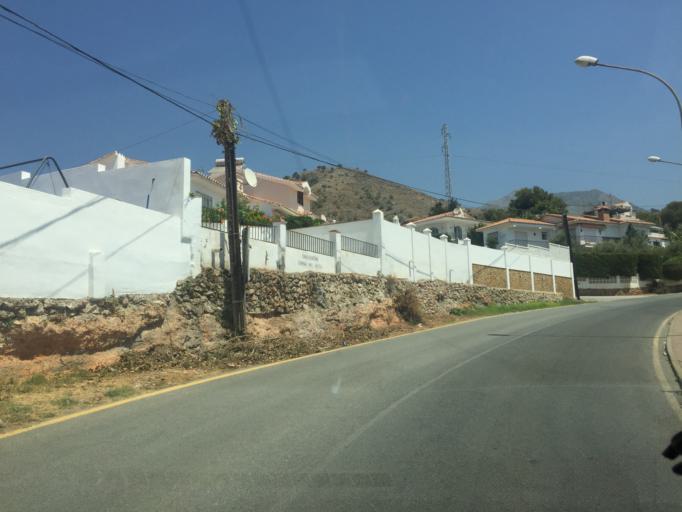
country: ES
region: Andalusia
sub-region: Provincia de Malaga
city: Nerja
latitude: 36.7610
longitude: -3.8484
